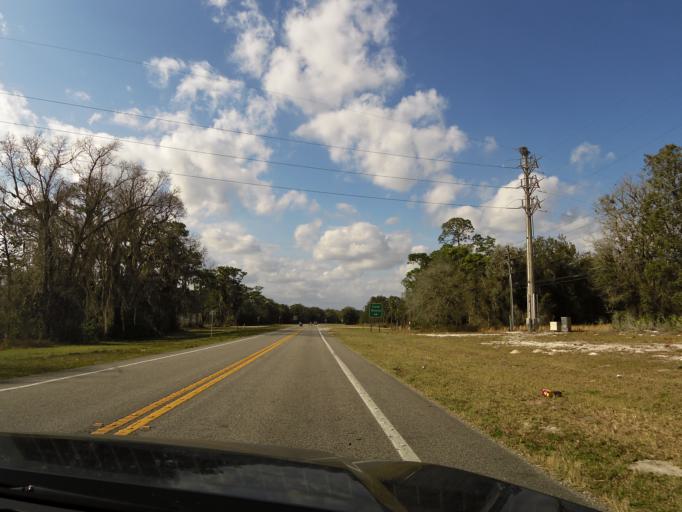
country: US
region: Florida
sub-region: Volusia County
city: De Leon Springs
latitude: 29.1393
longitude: -81.3582
